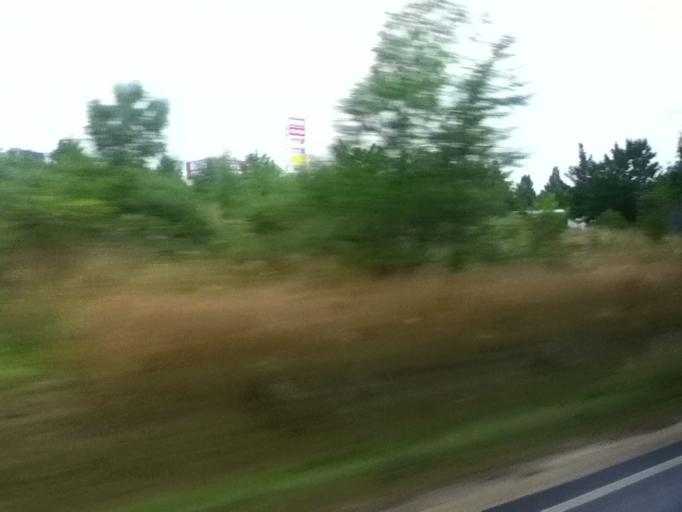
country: DE
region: Thuringia
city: Grossobringen
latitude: 51.0069
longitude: 11.3323
